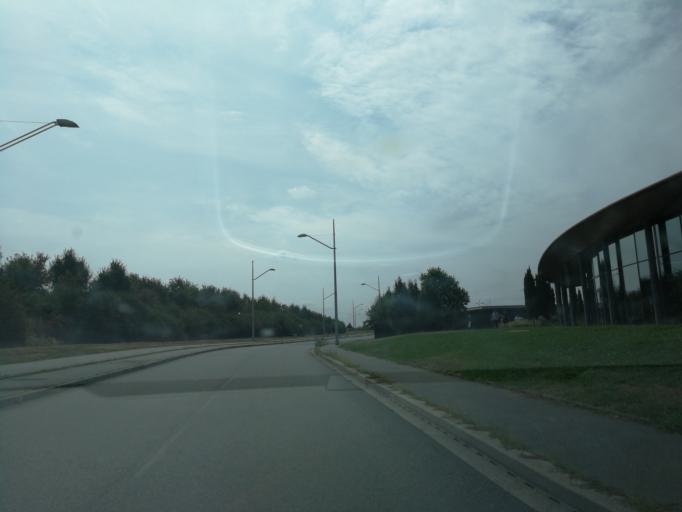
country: FR
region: Midi-Pyrenees
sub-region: Departement de la Haute-Garonne
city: Beauzelle
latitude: 43.6480
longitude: 1.3647
